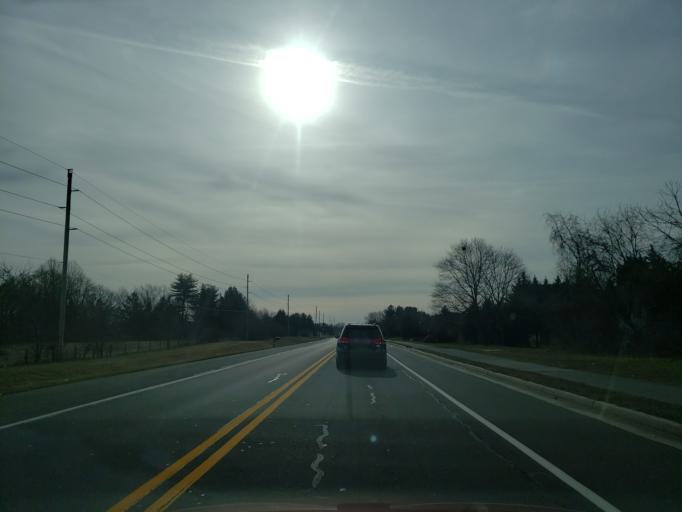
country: US
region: Delaware
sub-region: Kent County
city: Dover
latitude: 39.1809
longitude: -75.5587
